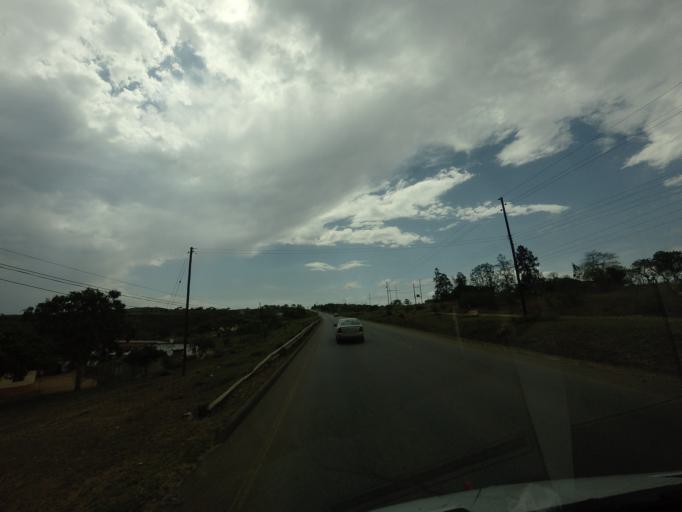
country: SZ
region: Manzini
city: Manzini
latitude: -26.5019
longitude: 31.4822
